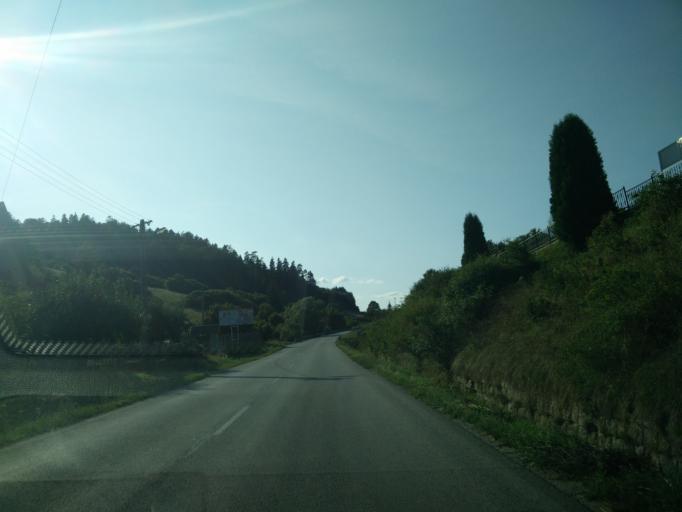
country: SK
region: Nitriansky
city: Prievidza
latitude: 48.8792
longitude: 18.7222
